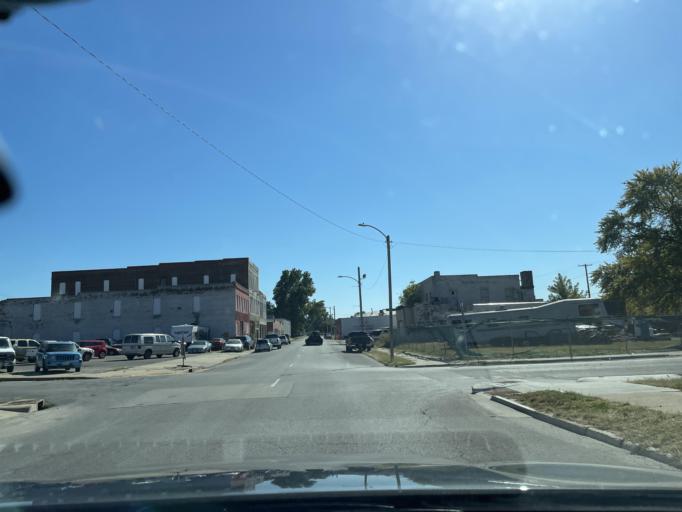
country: US
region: Missouri
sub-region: Buchanan County
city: Saint Joseph
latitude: 39.7592
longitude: -94.8494
